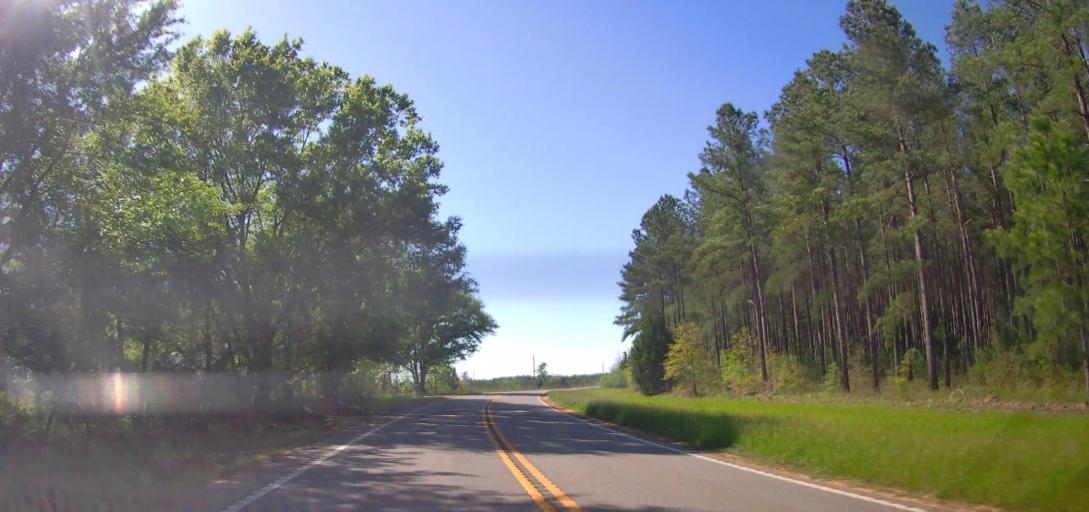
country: US
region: Georgia
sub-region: Dooly County
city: Unadilla
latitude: 32.2556
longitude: -83.6465
